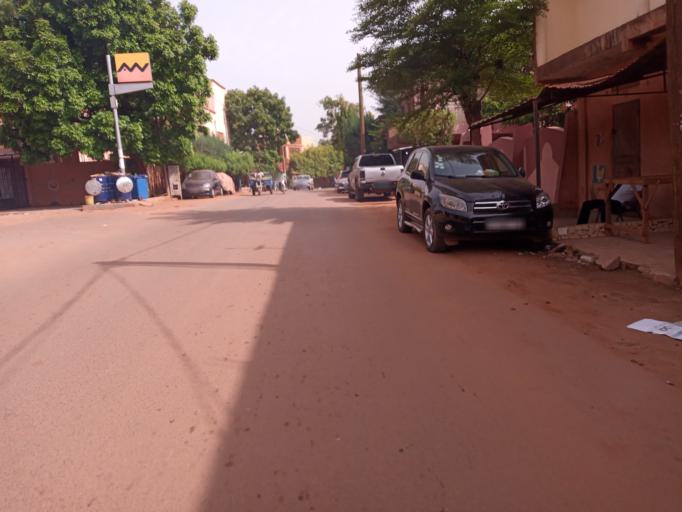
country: ML
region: Bamako
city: Bamako
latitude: 12.6061
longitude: -7.9513
